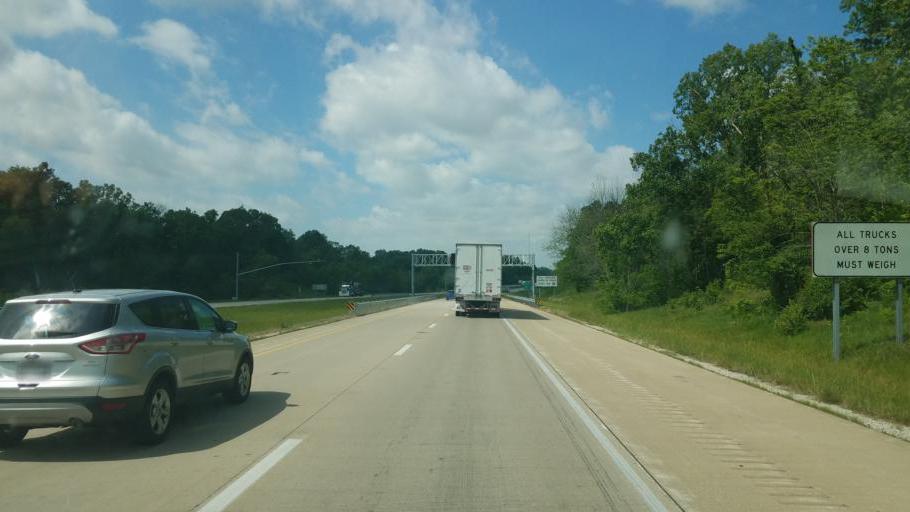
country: US
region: Indiana
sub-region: Vigo County
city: West Terre Haute
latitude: 39.4315
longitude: -87.5424
